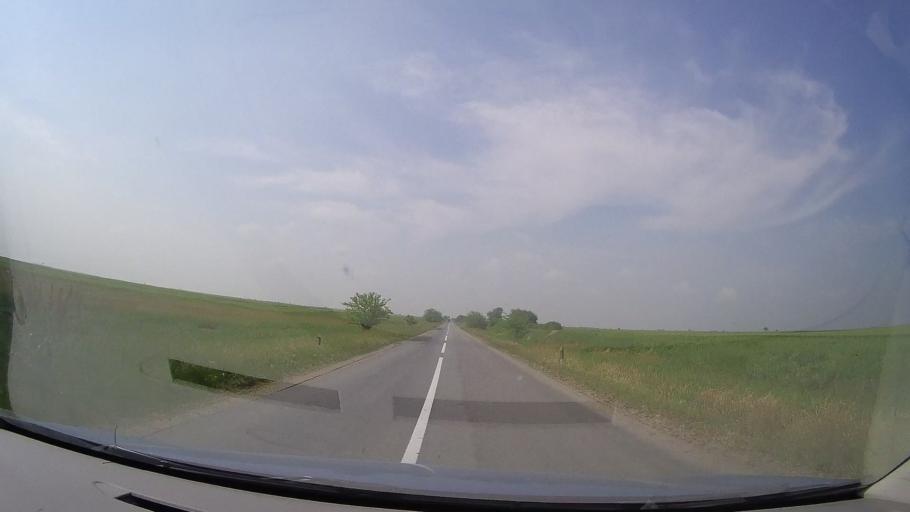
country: RS
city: Padina
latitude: 45.1594
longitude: 20.7495
